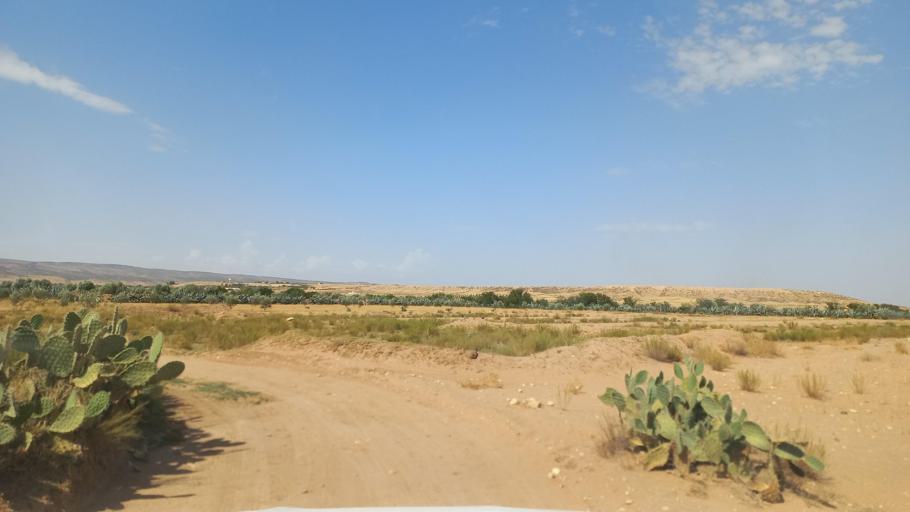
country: TN
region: Al Qasrayn
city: Kasserine
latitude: 35.2568
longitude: 8.9546
